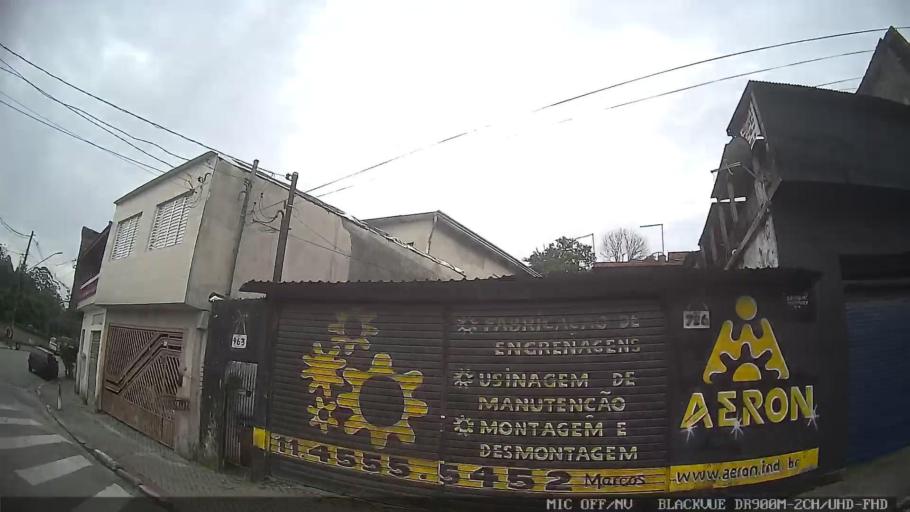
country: BR
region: Sao Paulo
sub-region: Maua
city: Maua
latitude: -23.6822
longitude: -46.4676
